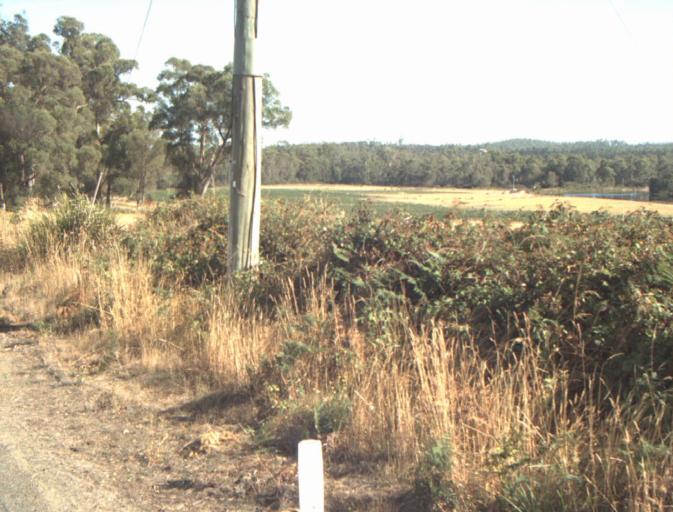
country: AU
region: Tasmania
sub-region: Dorset
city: Bridport
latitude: -41.1515
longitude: 147.2283
